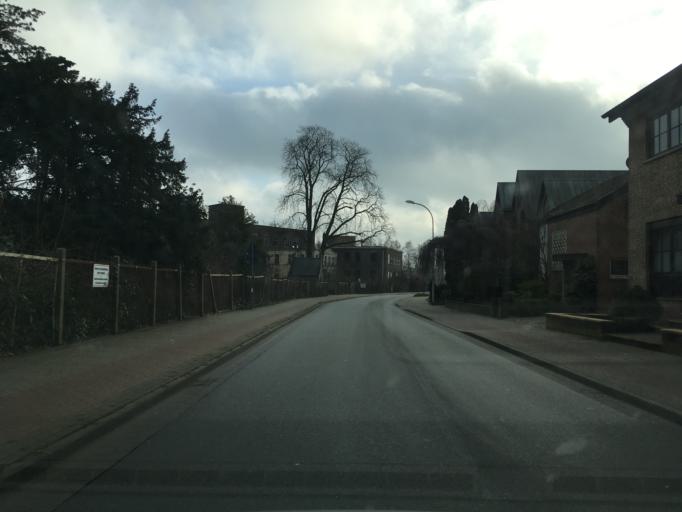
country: DE
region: North Rhine-Westphalia
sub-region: Regierungsbezirk Munster
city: Gronau
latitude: 52.2176
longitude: 7.0192
